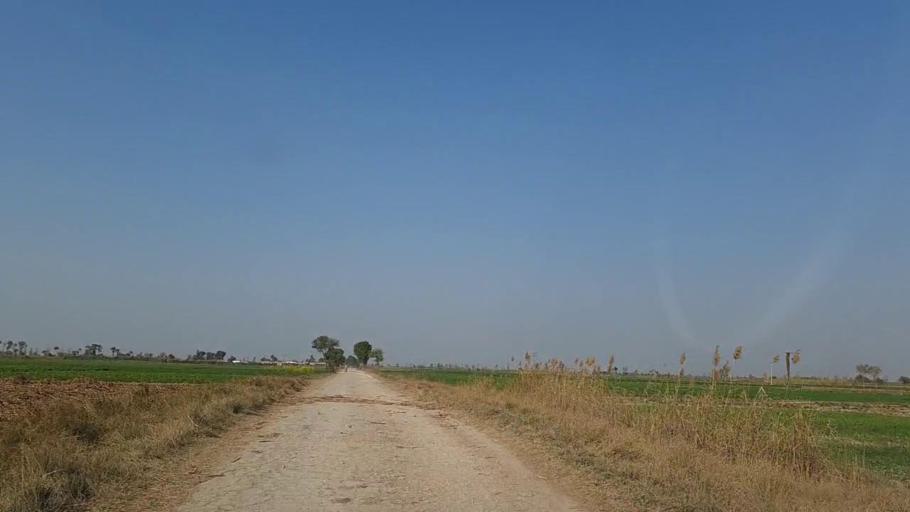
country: PK
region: Sindh
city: Daur
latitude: 26.4720
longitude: 68.2970
